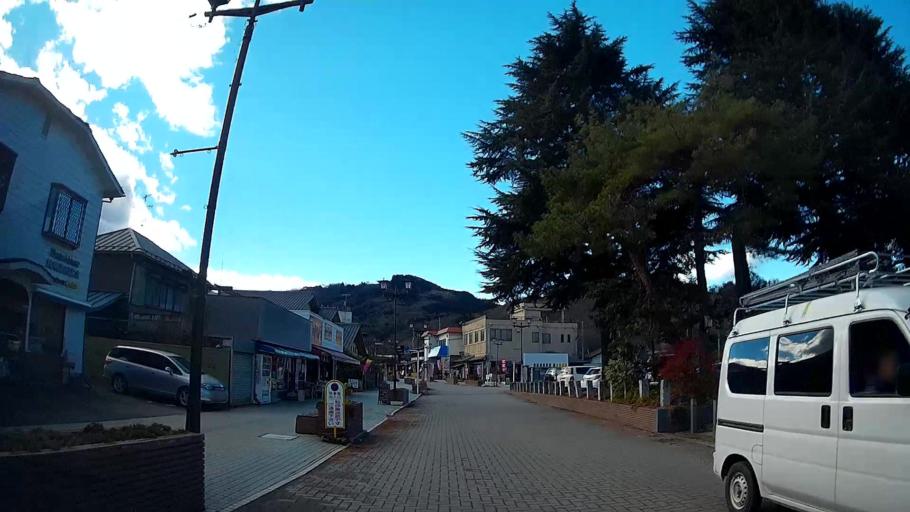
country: JP
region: Saitama
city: Yorii
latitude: 36.0943
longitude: 139.1120
